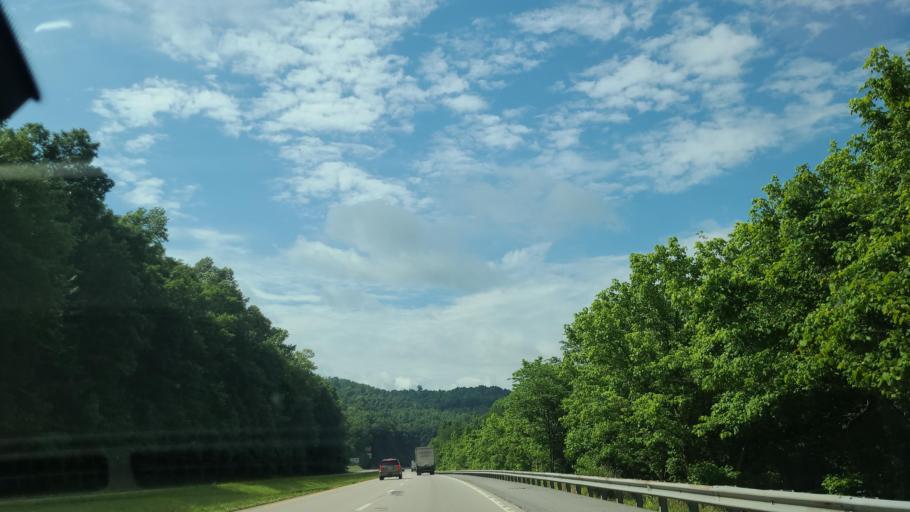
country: US
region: Kentucky
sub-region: Bell County
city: Middlesboro
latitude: 36.6510
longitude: -83.7009
